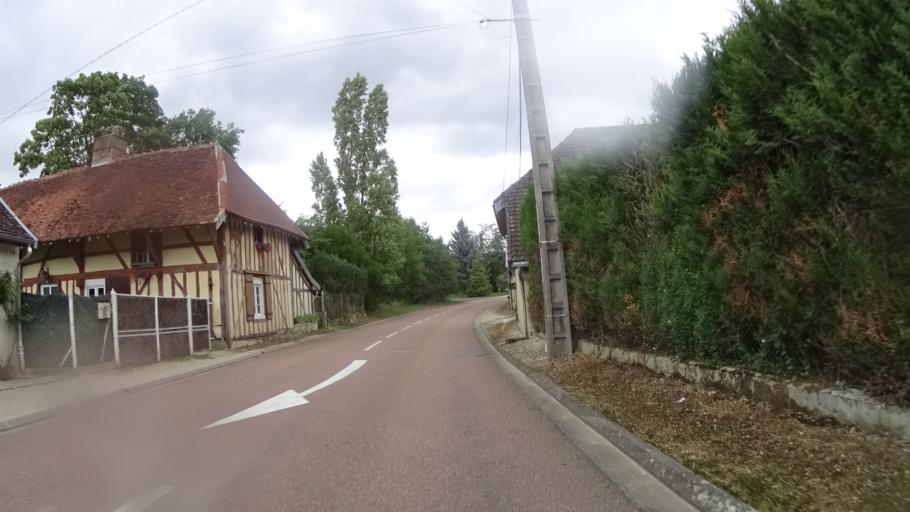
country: FR
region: Champagne-Ardenne
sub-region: Departement de l'Aube
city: Verrieres
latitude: 48.2442
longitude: 4.1793
